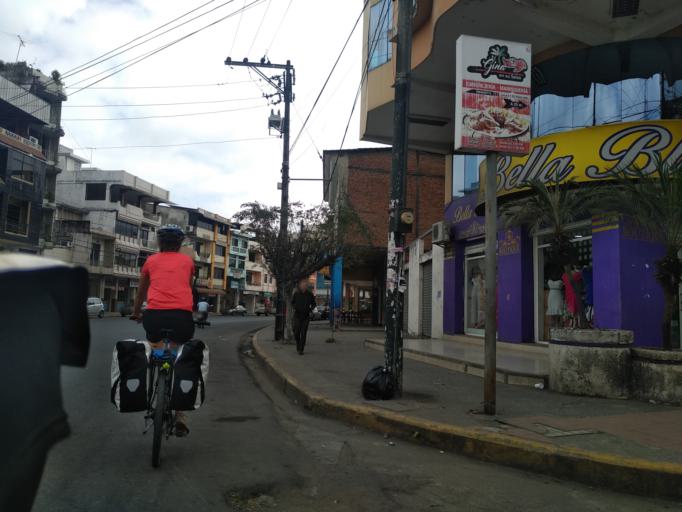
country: EC
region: Los Rios
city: Quevedo
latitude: -1.0303
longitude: -79.4688
